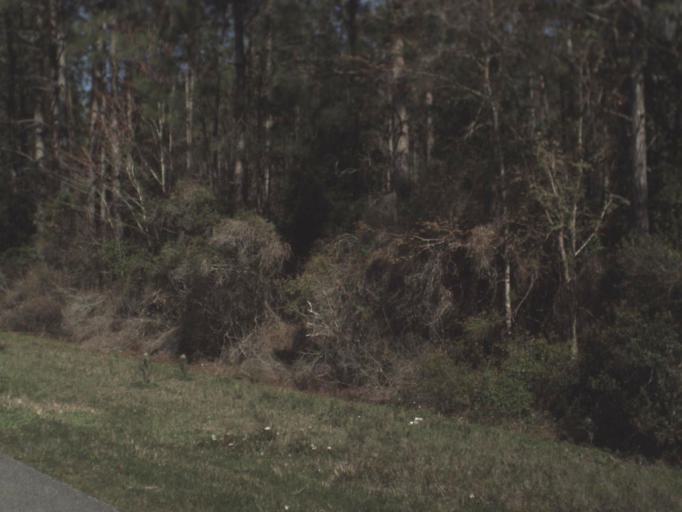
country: US
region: Florida
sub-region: Gulf County
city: Port Saint Joe
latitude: 29.8919
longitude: -85.2158
